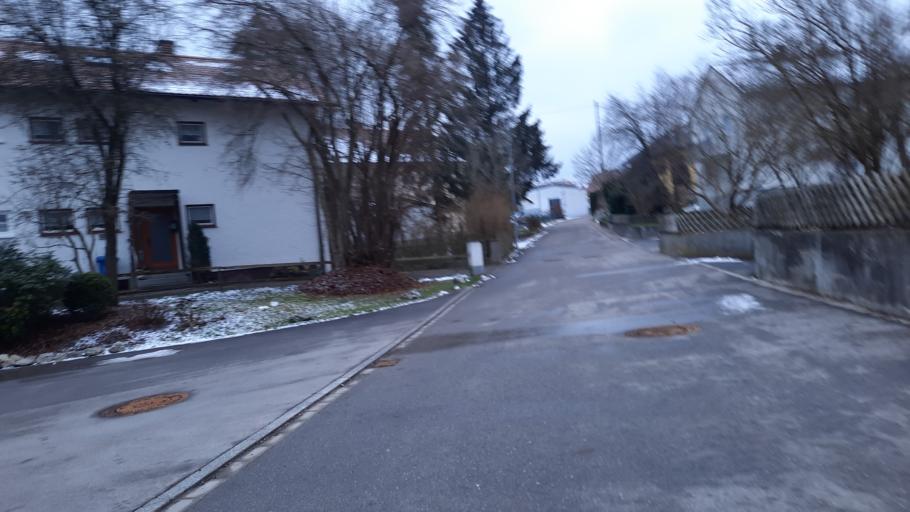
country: DE
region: Bavaria
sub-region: Swabia
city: Memmingen
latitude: 47.9556
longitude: 10.1696
